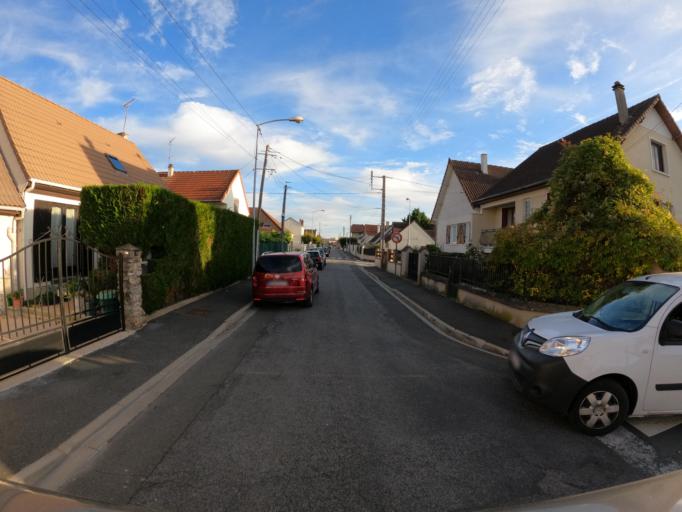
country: FR
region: Ile-de-France
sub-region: Departement de Seine-et-Marne
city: Pontault-Combault
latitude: 48.8084
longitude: 2.6071
